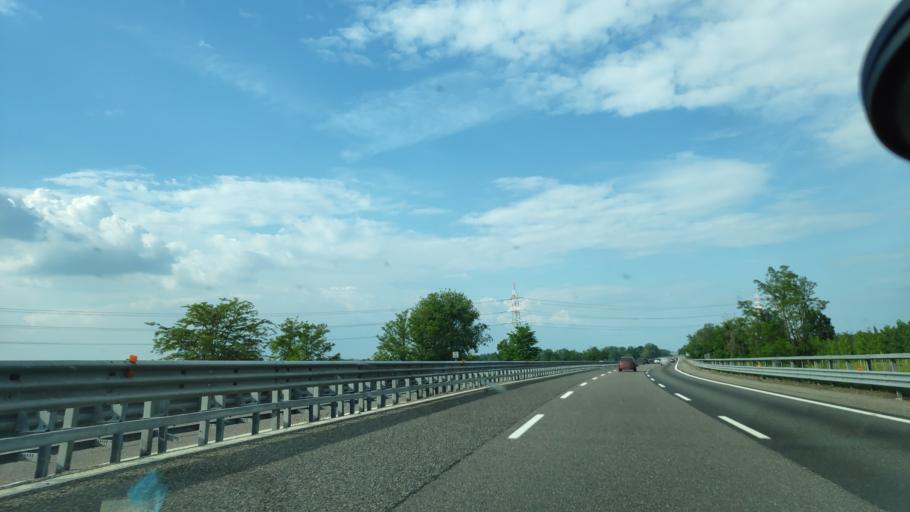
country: IT
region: Lombardy
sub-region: Provincia di Pavia
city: Zerbolo
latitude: 45.2187
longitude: 9.0189
